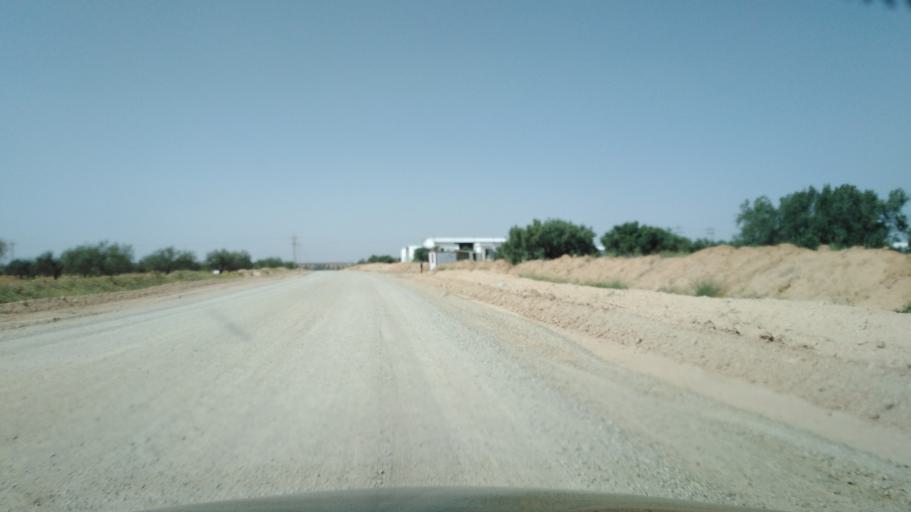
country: TN
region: Safaqis
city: Sfax
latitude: 34.7013
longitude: 10.4848
